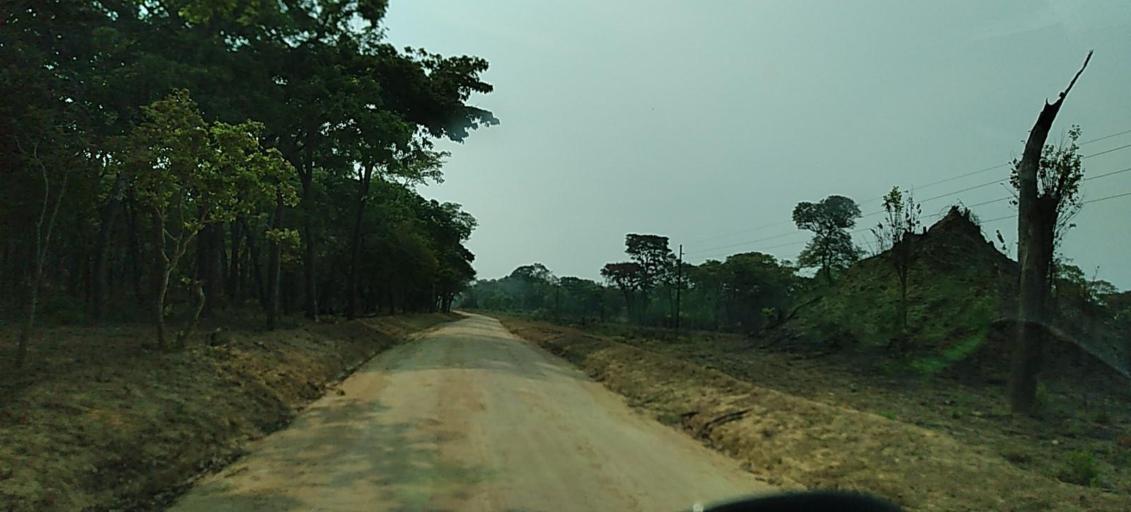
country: ZM
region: North-Western
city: Solwezi
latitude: -12.6932
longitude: 26.4028
